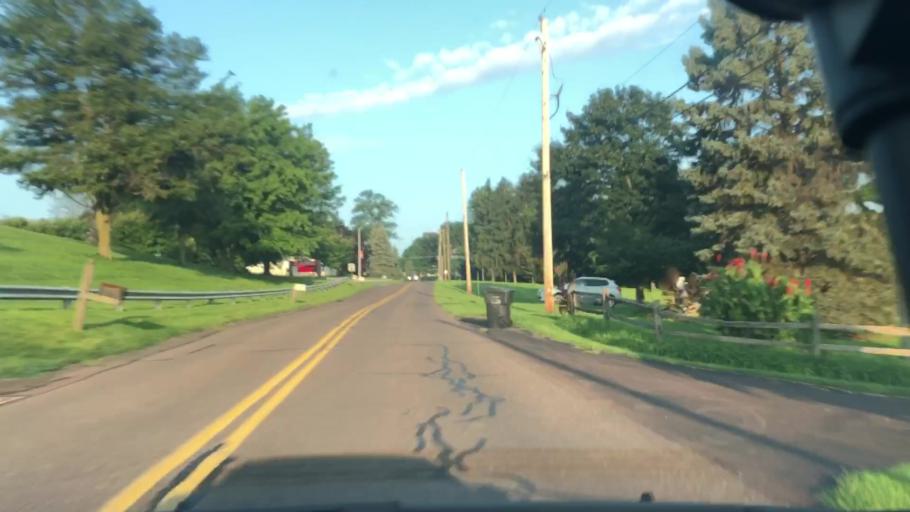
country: US
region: Pennsylvania
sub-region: Chester County
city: Kenilworth
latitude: 40.1795
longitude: -75.6578
